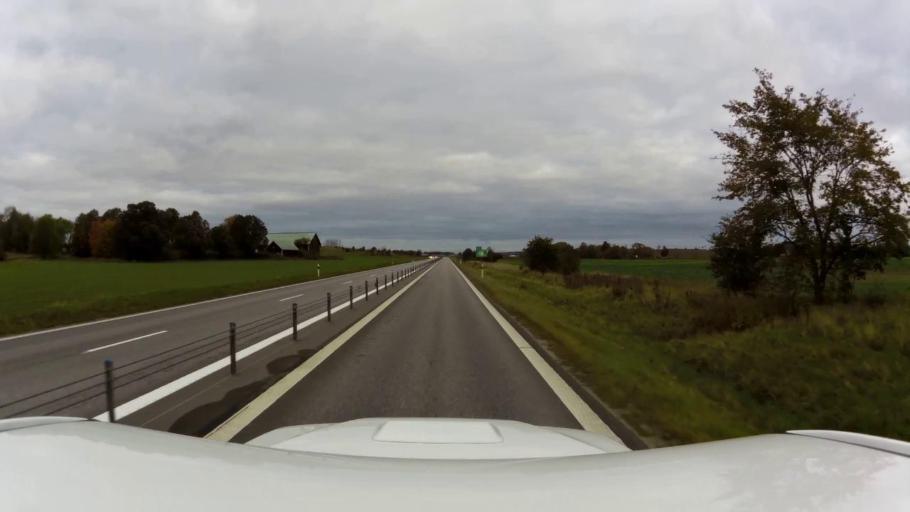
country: SE
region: OEstergoetland
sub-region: Linkopings Kommun
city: Berg
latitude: 58.4711
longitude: 15.4919
